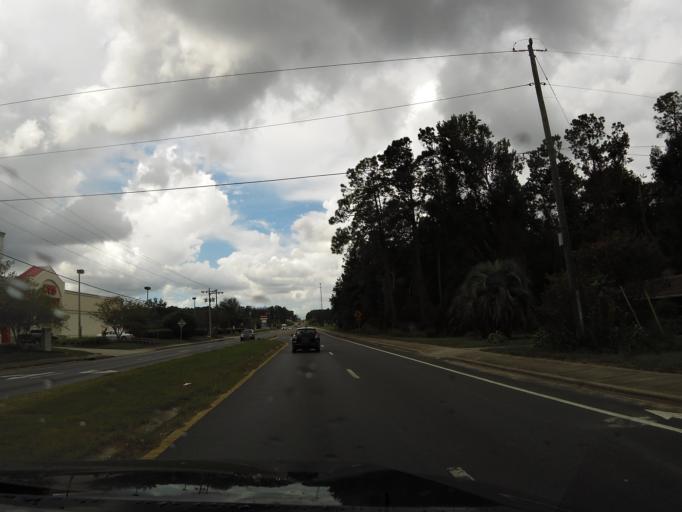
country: US
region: Florida
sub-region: Clay County
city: Middleburg
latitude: 30.0630
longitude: -81.8748
